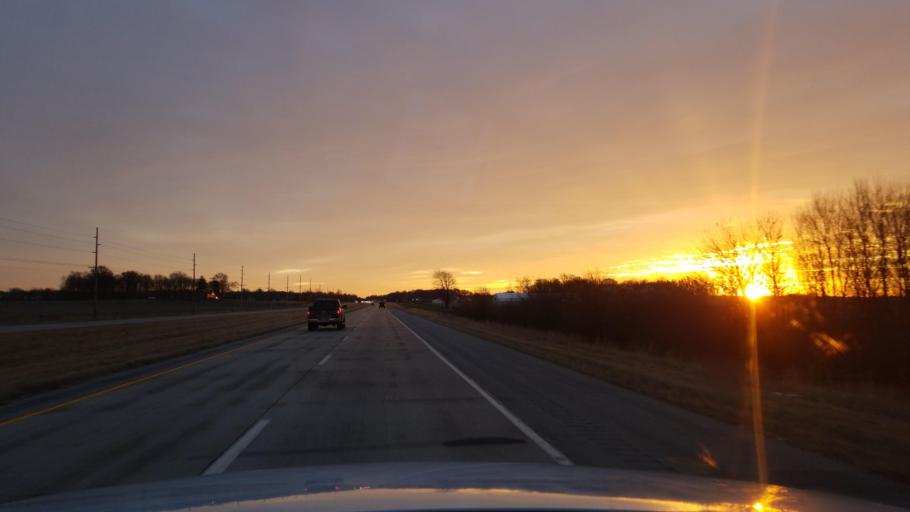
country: US
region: Indiana
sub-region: Posey County
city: Mount Vernon
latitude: 37.9420
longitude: -87.7704
